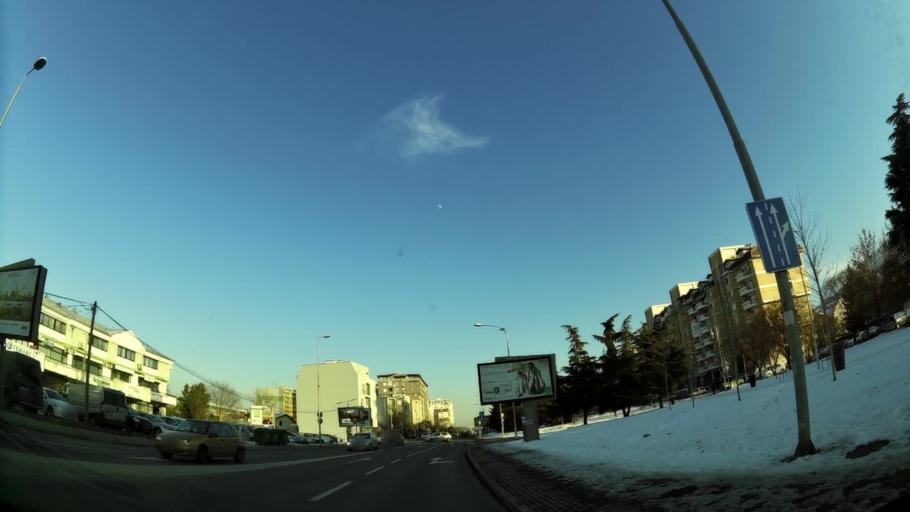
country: MK
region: Karpos
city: Skopje
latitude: 41.9981
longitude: 21.3917
